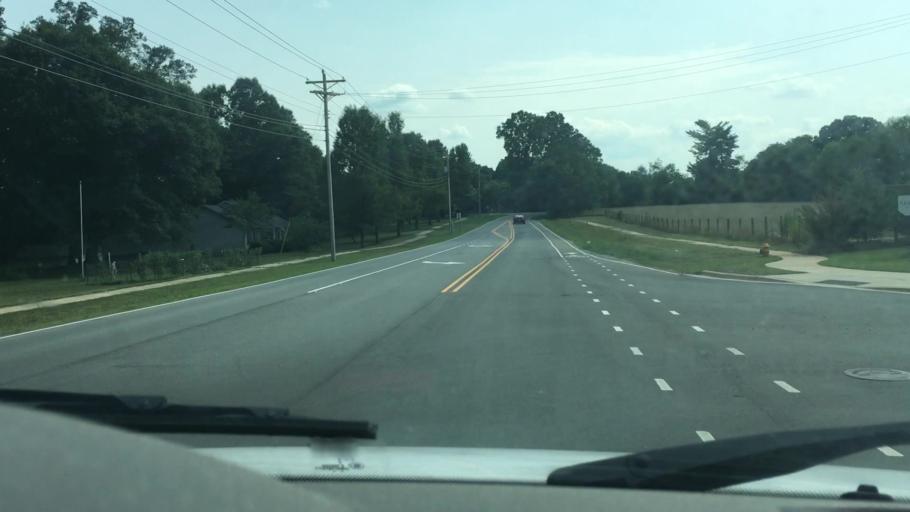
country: US
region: North Carolina
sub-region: Mecklenburg County
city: Huntersville
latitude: 35.4039
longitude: -80.9123
